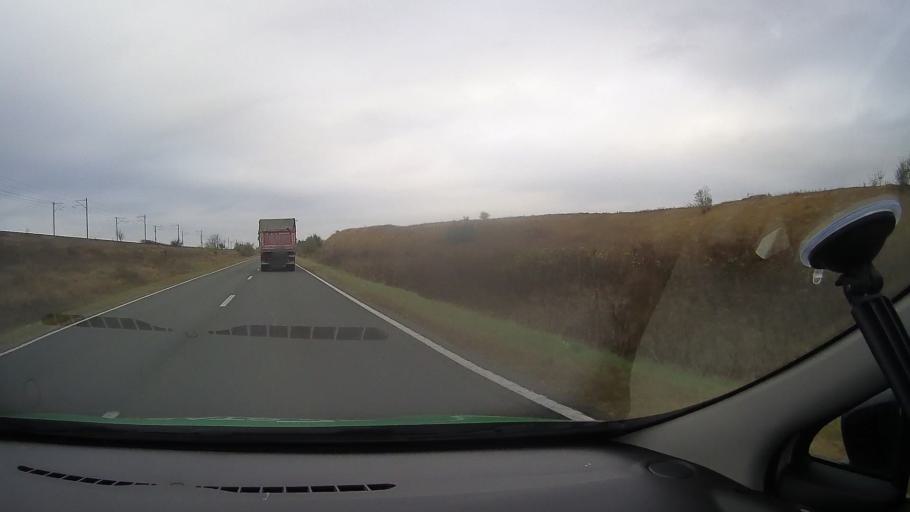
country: RO
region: Constanta
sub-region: Comuna Poarta Alba
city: Poarta Alba
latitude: 44.2233
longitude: 28.3856
